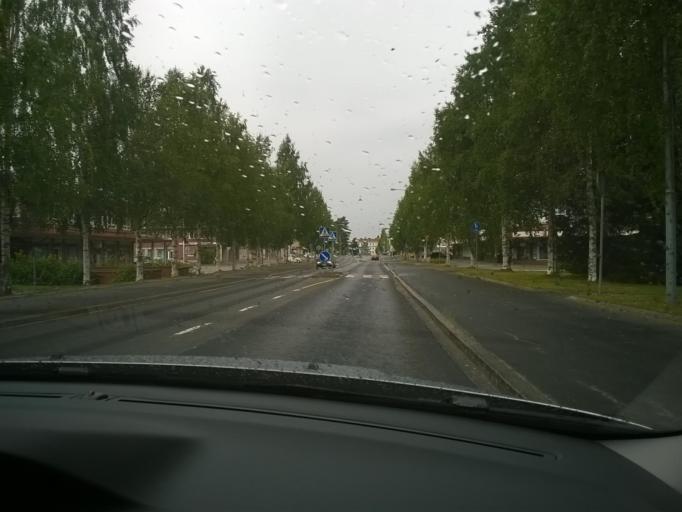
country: FI
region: Kainuu
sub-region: Kehys-Kainuu
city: Kuhmo
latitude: 64.1263
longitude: 29.5267
